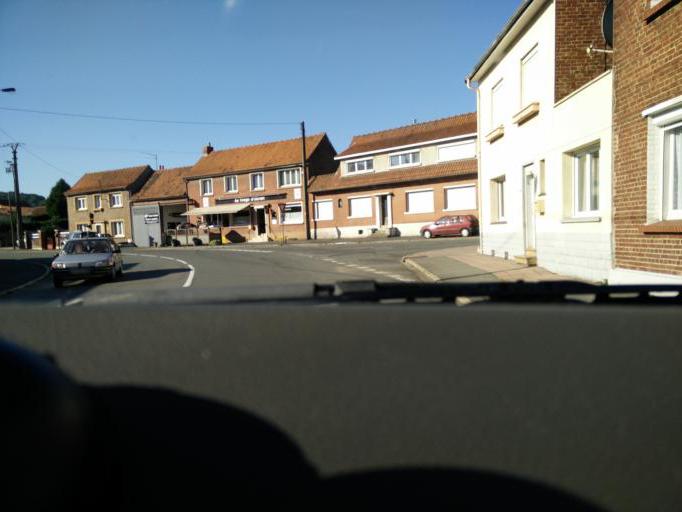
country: FR
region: Nord-Pas-de-Calais
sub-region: Departement du Pas-de-Calais
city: Divion
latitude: 50.4556
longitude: 2.4806
